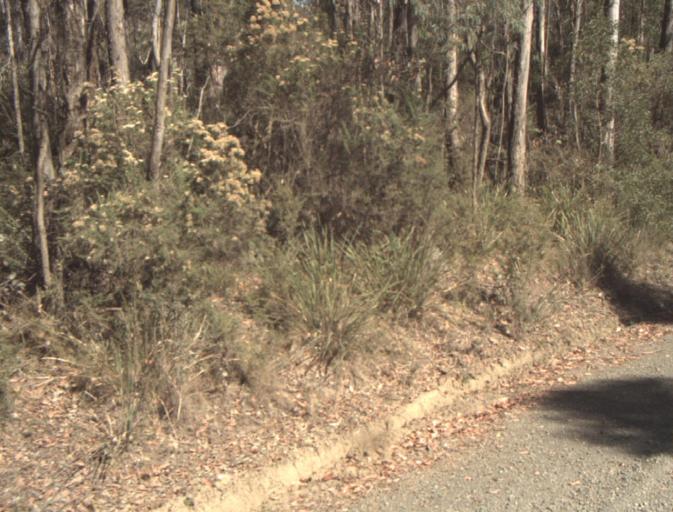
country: AU
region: Tasmania
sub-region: Launceston
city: Newstead
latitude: -41.3647
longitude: 147.2319
